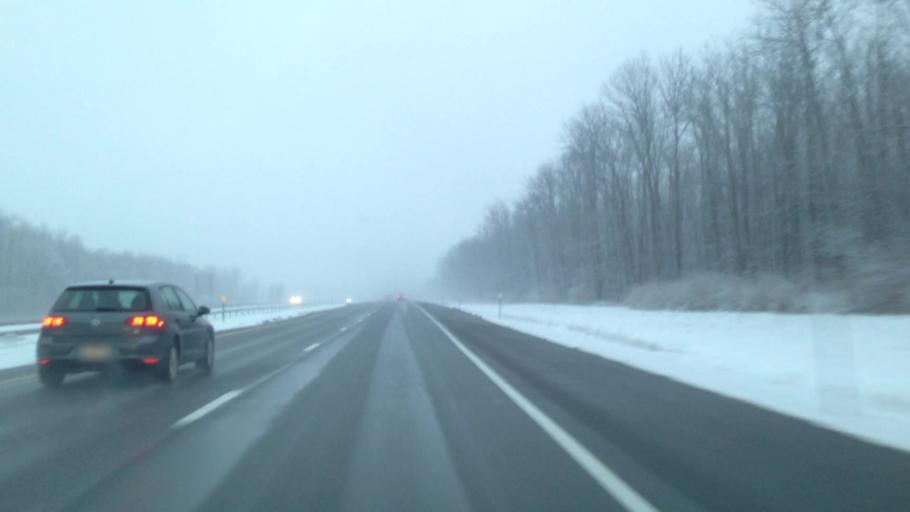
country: US
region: New York
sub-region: Madison County
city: Canastota
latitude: 43.0938
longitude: -75.8012
